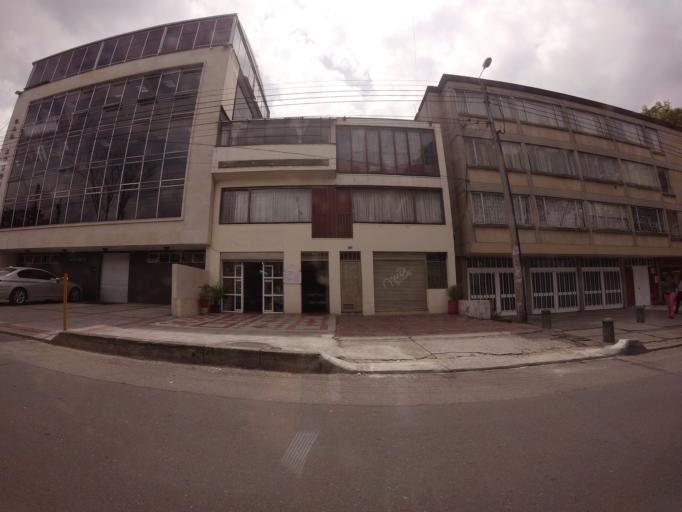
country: CO
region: Bogota D.C.
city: Bogota
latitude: 4.6298
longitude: -74.0784
